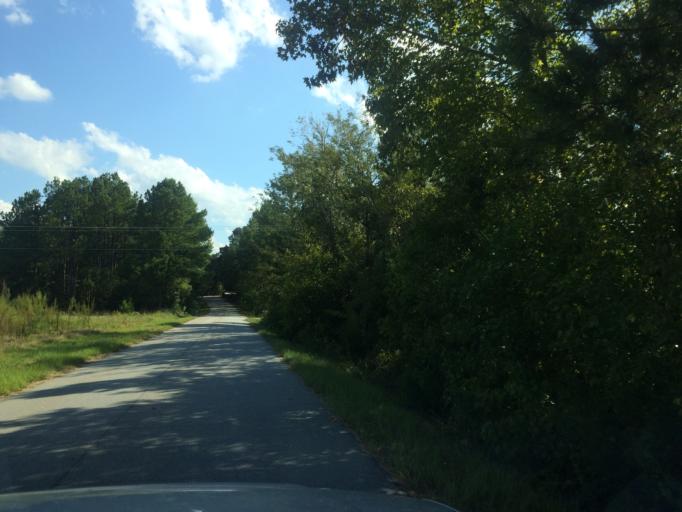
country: US
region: South Carolina
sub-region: Greenwood County
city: Ware Shoals
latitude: 34.4639
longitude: -82.1772
